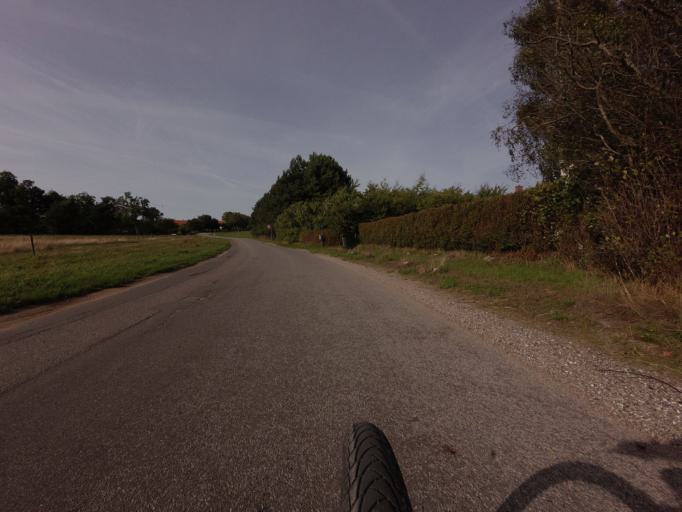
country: DK
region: Zealand
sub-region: Faxe Kommune
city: Fakse
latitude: 55.1845
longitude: 12.1128
